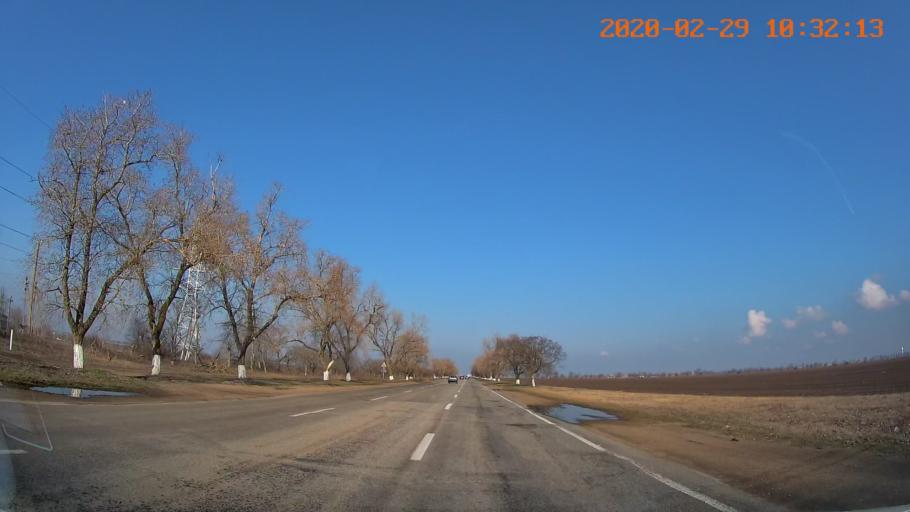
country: UA
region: Odessa
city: Velykoploske
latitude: 46.9584
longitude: 29.5556
